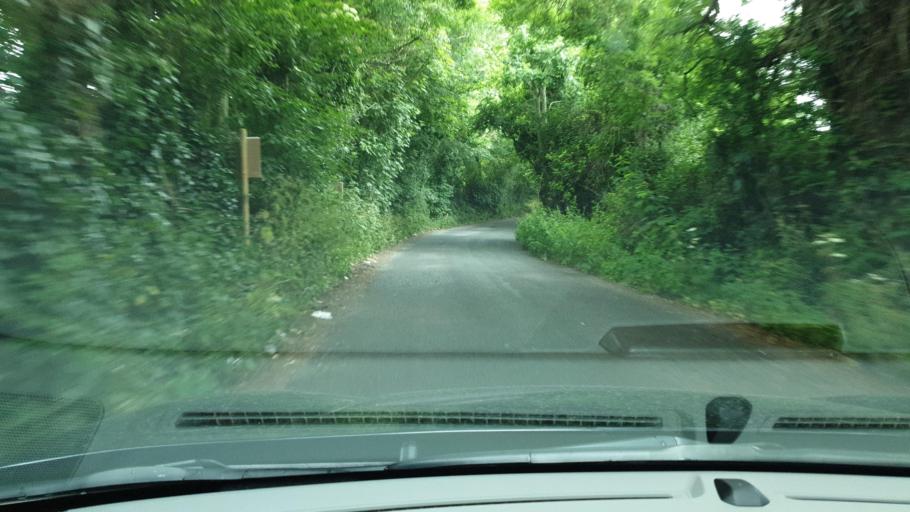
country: IE
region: Leinster
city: Hartstown
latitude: 53.4179
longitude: -6.4027
